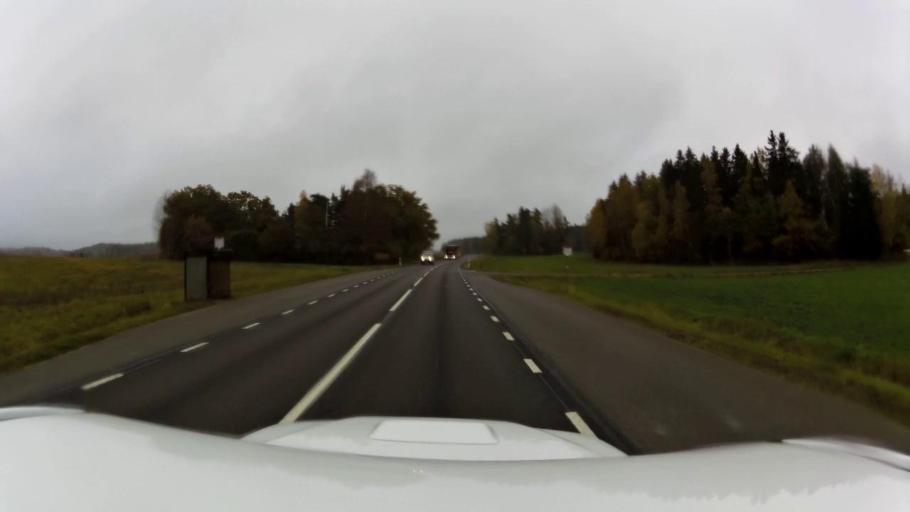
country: SE
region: OEstergoetland
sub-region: Linkopings Kommun
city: Linghem
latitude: 58.3688
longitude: 15.8188
